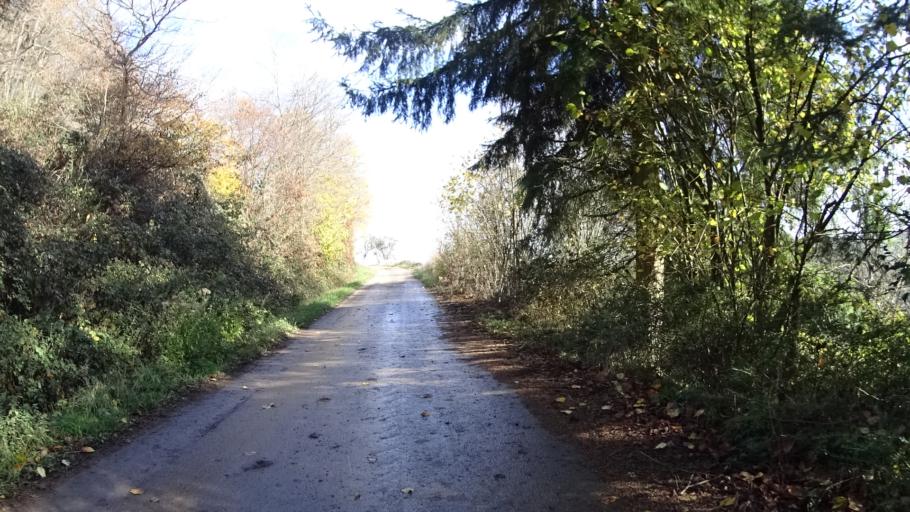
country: DE
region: Rheinland-Pfalz
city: Kirrweiler
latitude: 49.6317
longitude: 7.4943
